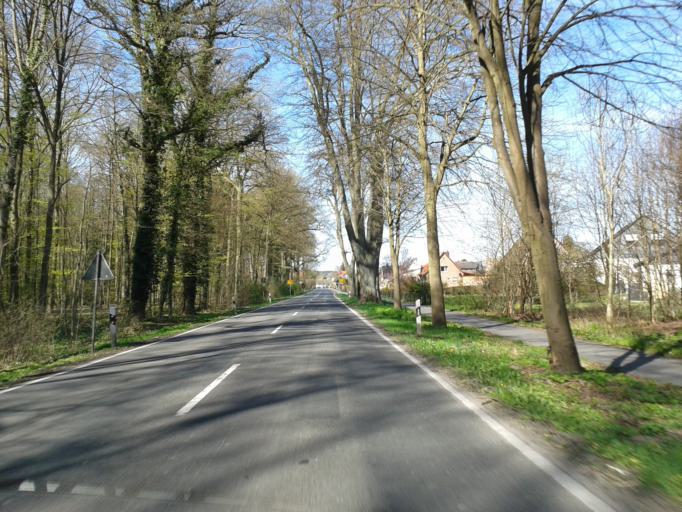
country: DE
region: Lower Saxony
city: Clenze
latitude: 52.9366
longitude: 10.9648
